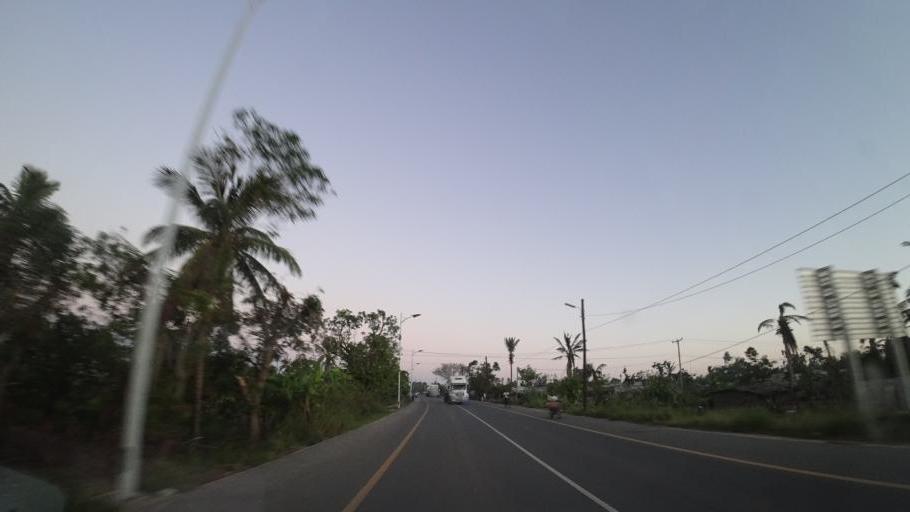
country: MZ
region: Sofala
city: Dondo
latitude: -19.5320
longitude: 34.6293
